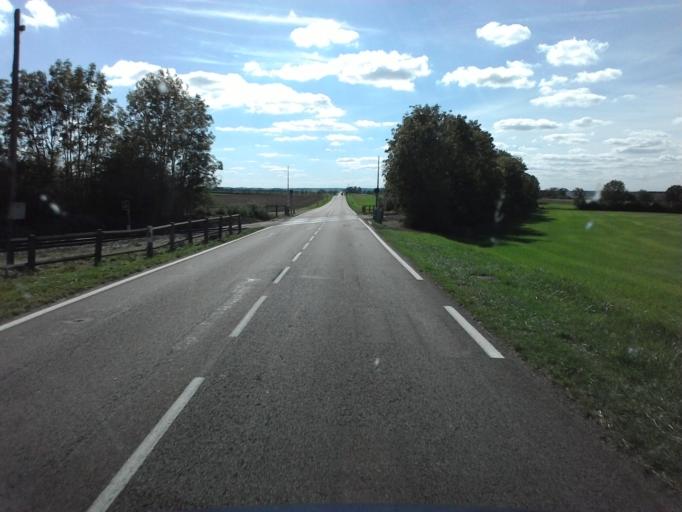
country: FR
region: Bourgogne
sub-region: Departement de la Cote-d'Or
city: Chatillon-sur-Seine
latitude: 47.8935
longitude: 4.6080
